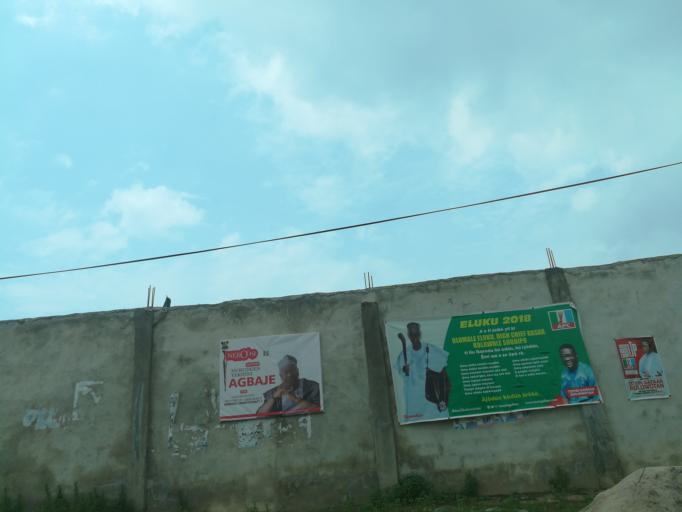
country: NG
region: Lagos
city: Ikorodu
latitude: 6.6144
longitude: 3.5122
